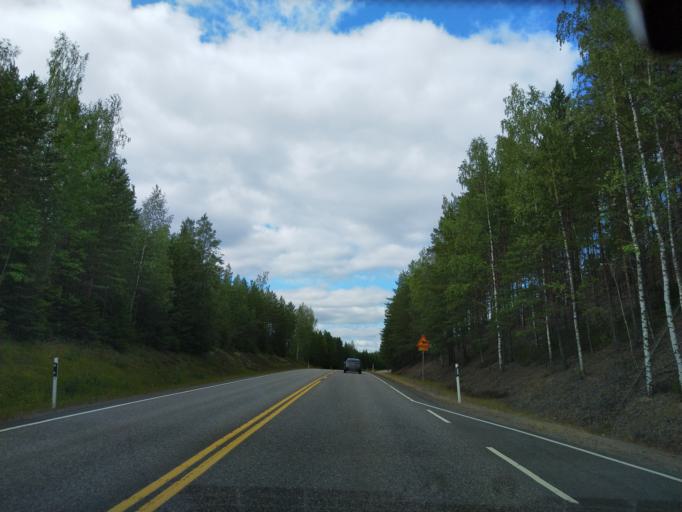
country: FI
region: Haeme
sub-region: Riihimaeki
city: Loppi
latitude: 60.7437
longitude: 24.3554
